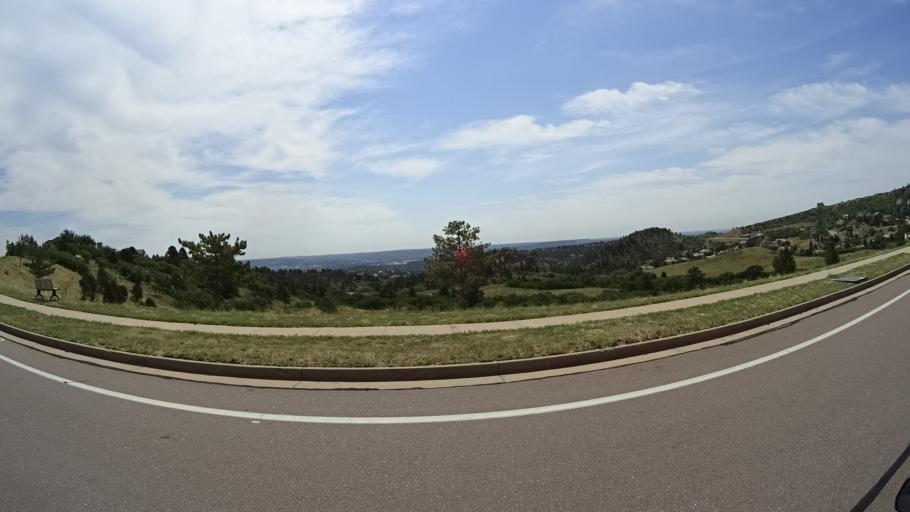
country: US
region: Colorado
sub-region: El Paso County
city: Air Force Academy
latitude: 38.9521
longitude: -104.8831
